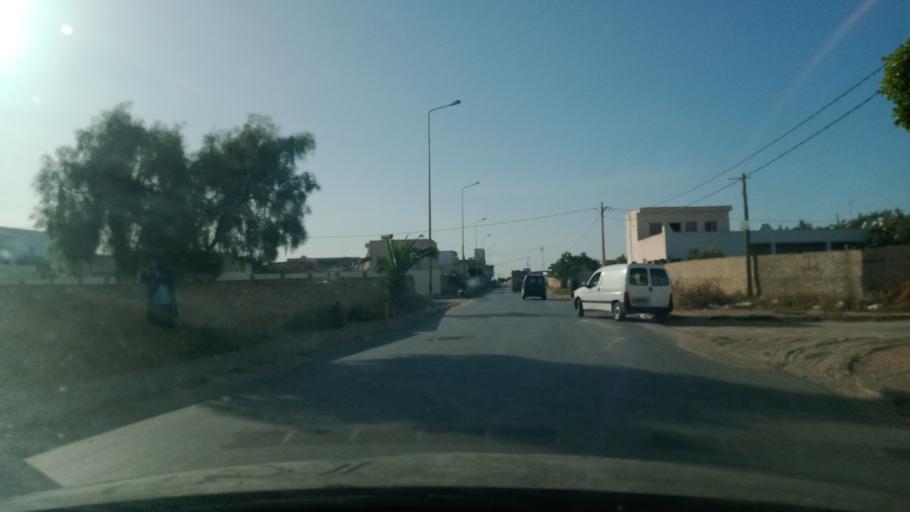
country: TN
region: Safaqis
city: Al Qarmadah
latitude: 34.8194
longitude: 10.7425
